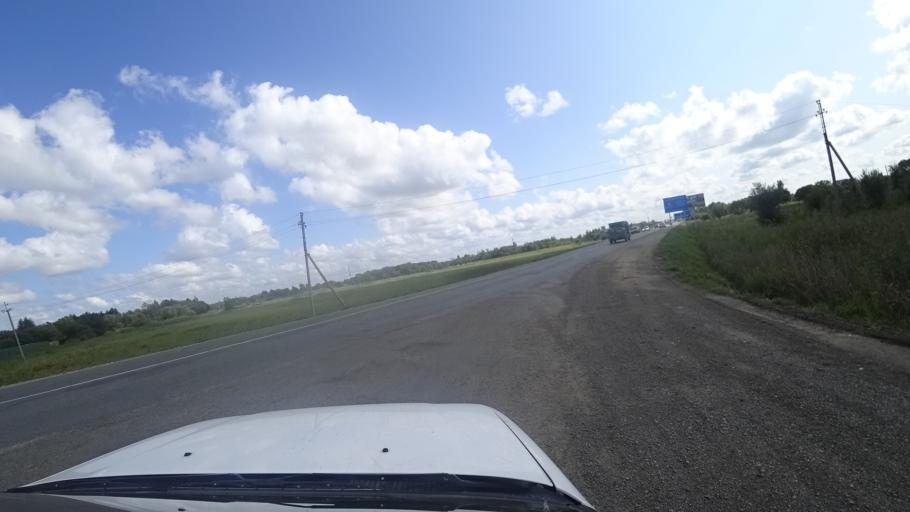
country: RU
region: Primorskiy
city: Dal'nerechensk
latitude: 45.9239
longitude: 133.7735
